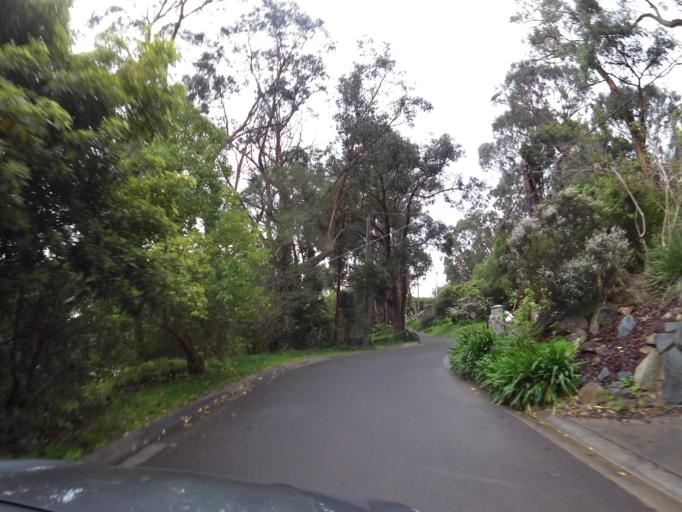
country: AU
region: Victoria
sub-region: Knox
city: The Basin
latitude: -37.8638
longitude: 145.3112
